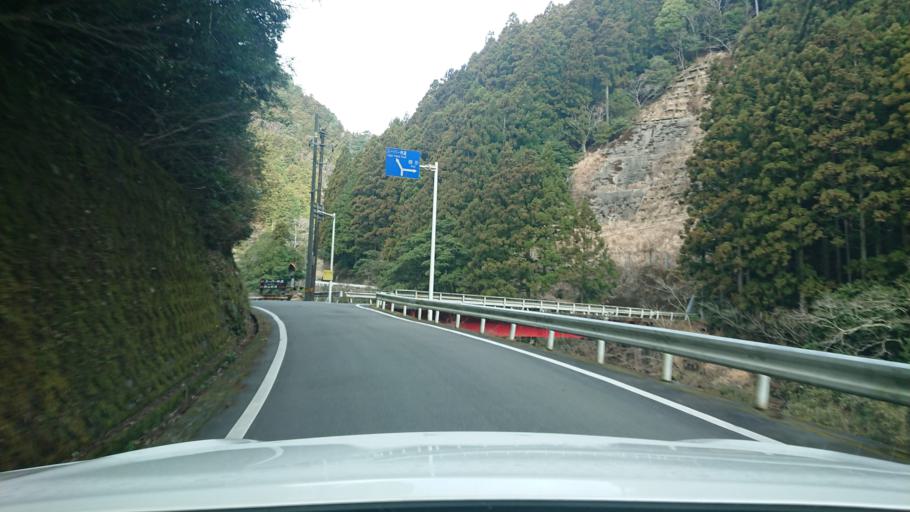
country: JP
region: Tokushima
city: Ishii
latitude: 33.9062
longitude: 134.3963
